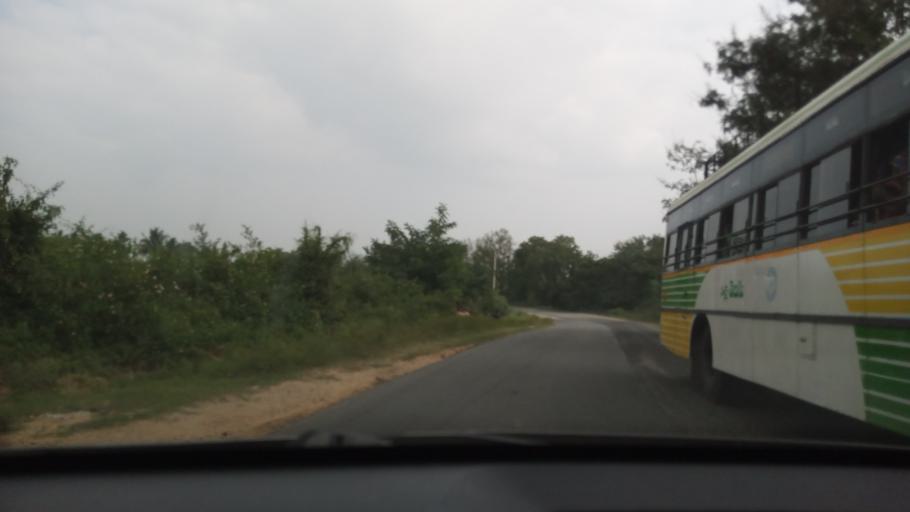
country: IN
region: Andhra Pradesh
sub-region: Chittoor
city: Pakala
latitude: 13.6562
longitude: 78.8396
